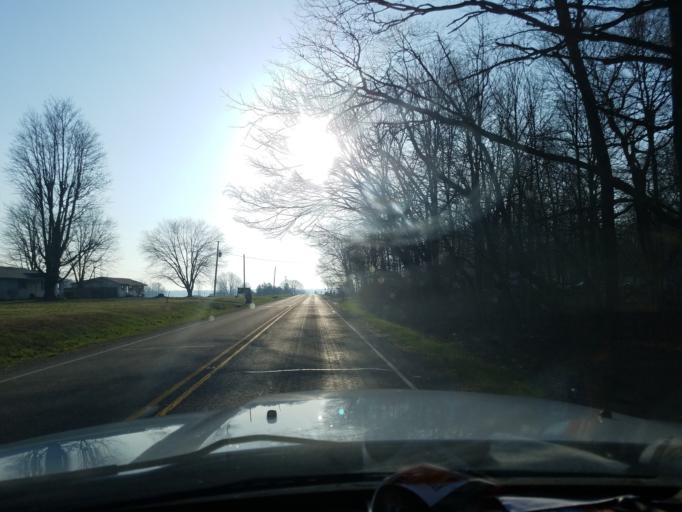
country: US
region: Indiana
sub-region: Clay County
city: Middlebury
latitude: 39.3879
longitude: -87.1639
